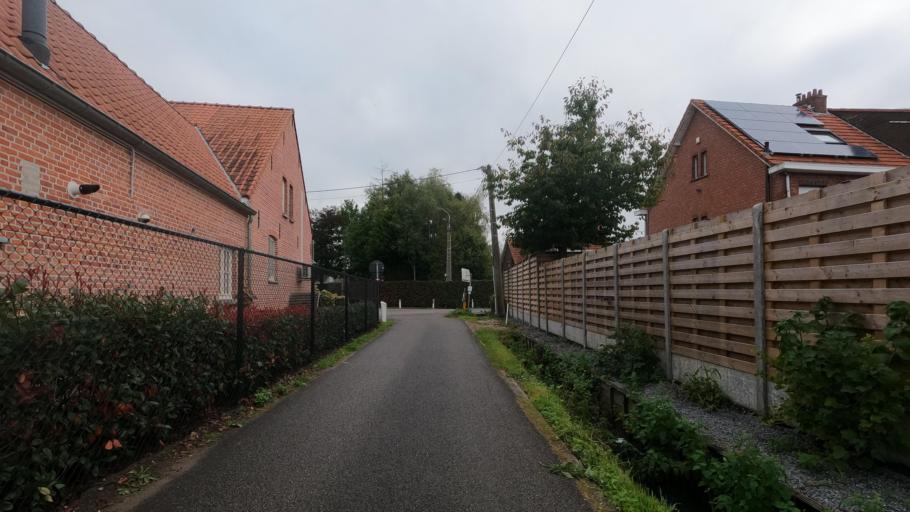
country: BE
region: Flanders
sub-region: Provincie Antwerpen
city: Schilde
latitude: 51.2645
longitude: 4.6306
